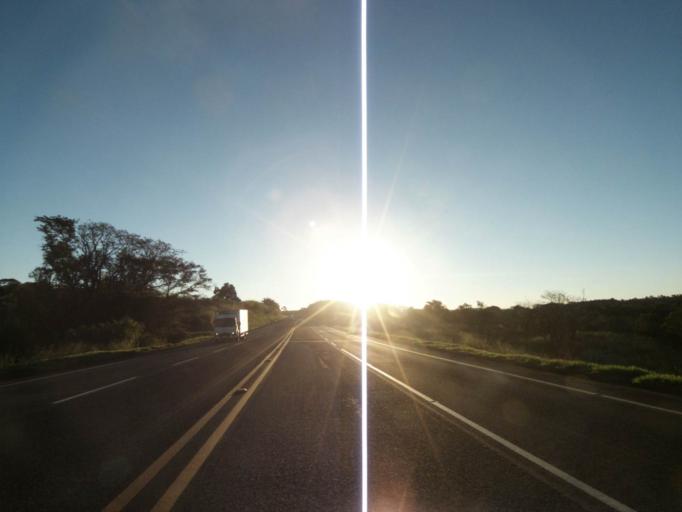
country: BR
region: Parana
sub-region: Mandaguari
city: Mandaguari
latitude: -23.4864
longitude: -51.6053
